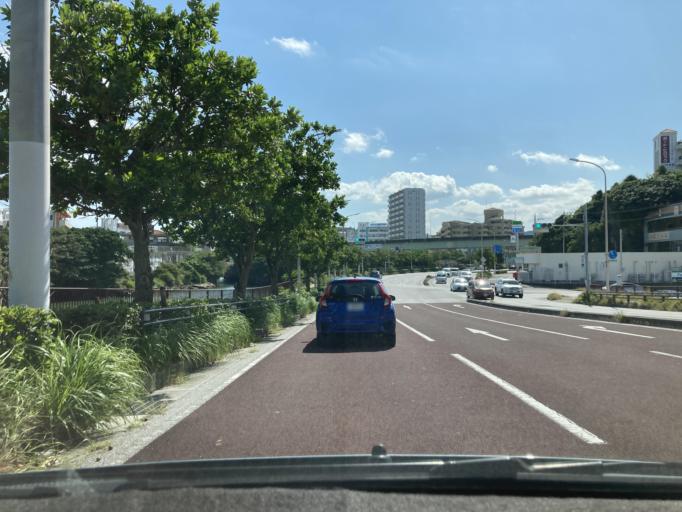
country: JP
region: Okinawa
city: Ginowan
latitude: 26.2693
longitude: 127.7262
